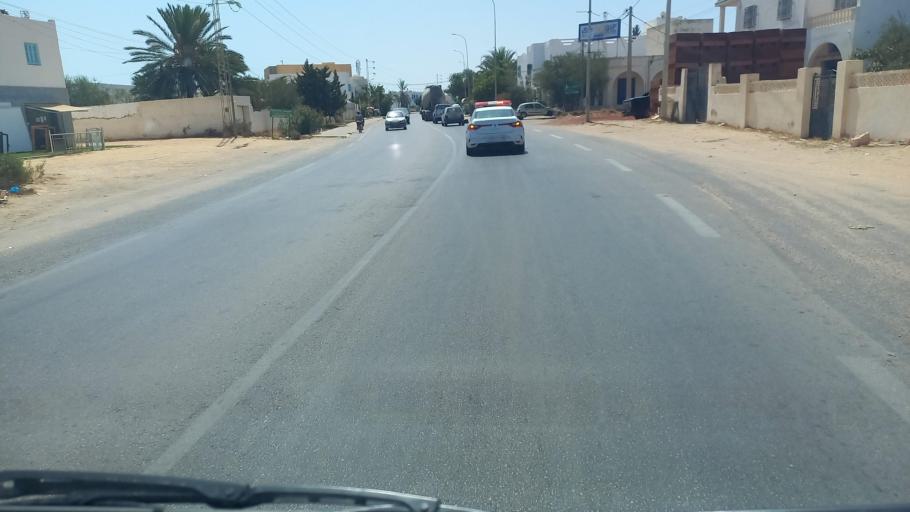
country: TN
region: Madanin
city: Houmt Souk
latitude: 33.8052
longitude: 10.8817
